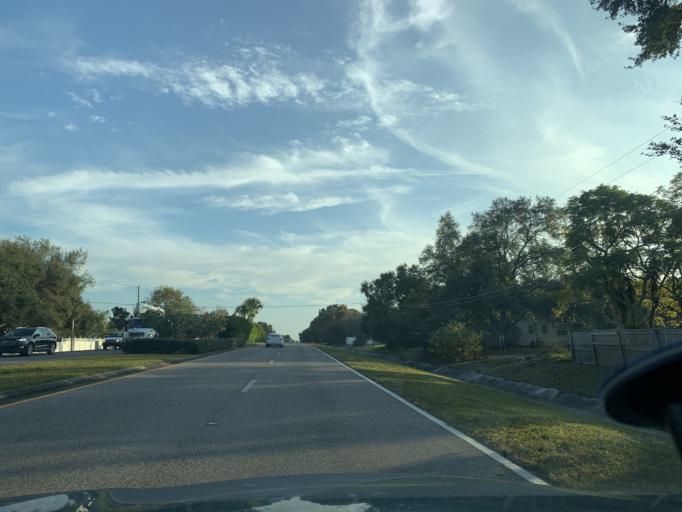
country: US
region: Florida
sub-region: Pinellas County
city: Ridgecrest
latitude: 27.8790
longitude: -82.7953
